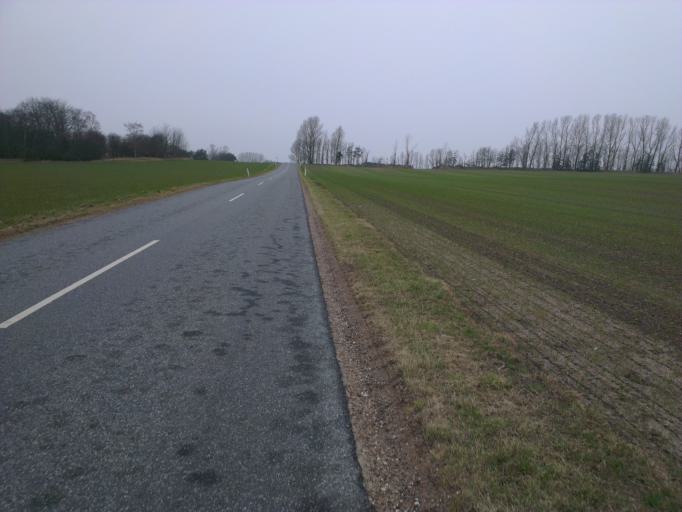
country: DK
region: Capital Region
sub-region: Frederikssund Kommune
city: Skibby
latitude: 55.7865
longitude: 12.0087
